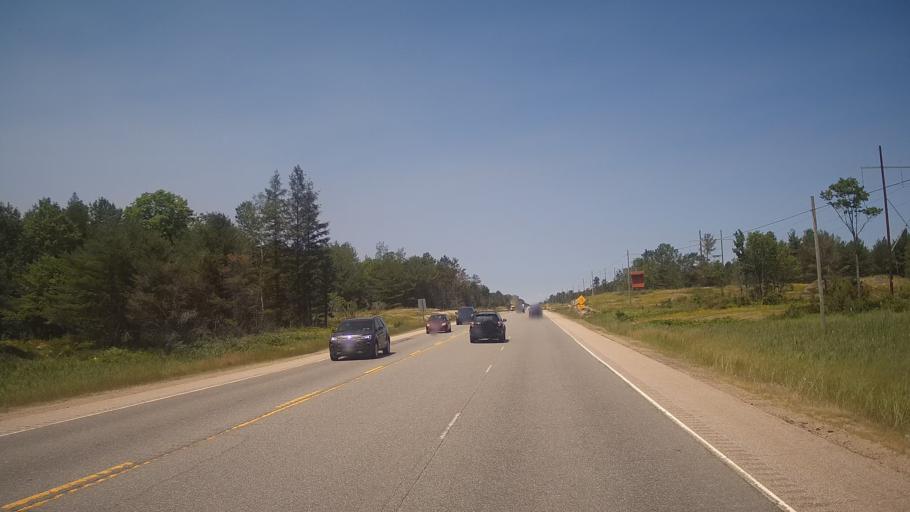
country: CA
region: Ontario
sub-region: Parry Sound District
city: Parry Sound
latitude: 45.5069
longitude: -80.2223
